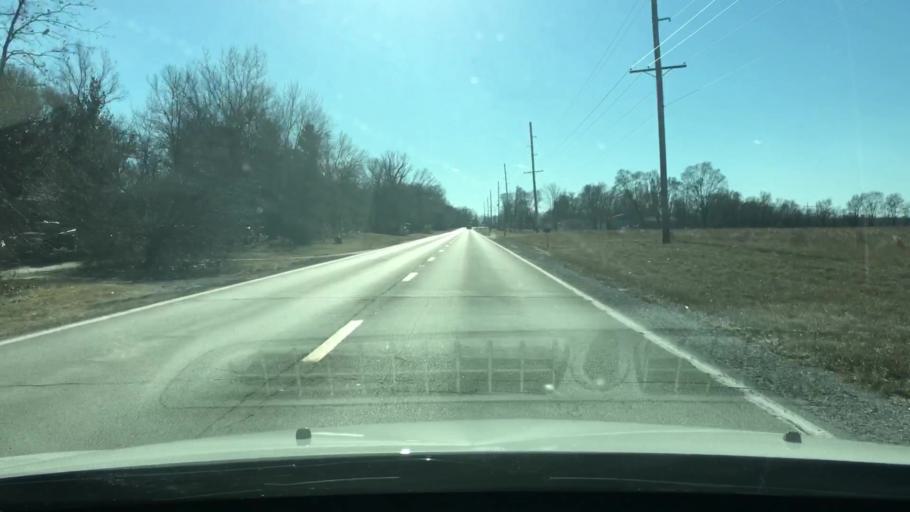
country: US
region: Illinois
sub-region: Cass County
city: Beardstown
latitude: 39.9494
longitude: -90.4853
